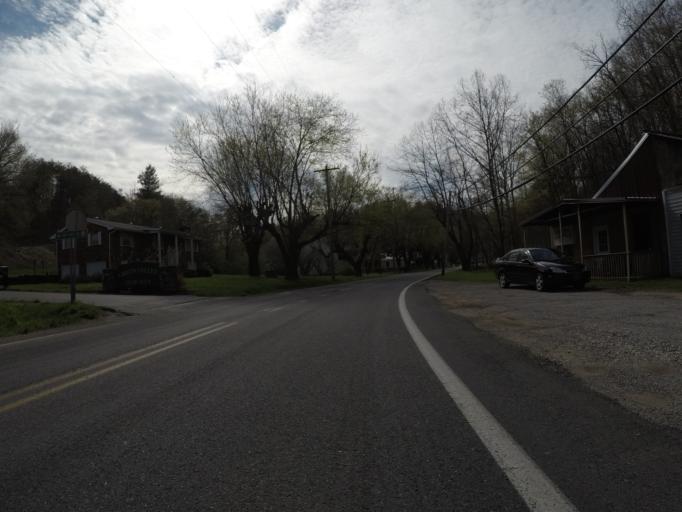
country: US
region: West Virginia
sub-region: Cabell County
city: Pea Ridge
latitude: 38.3758
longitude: -82.3713
